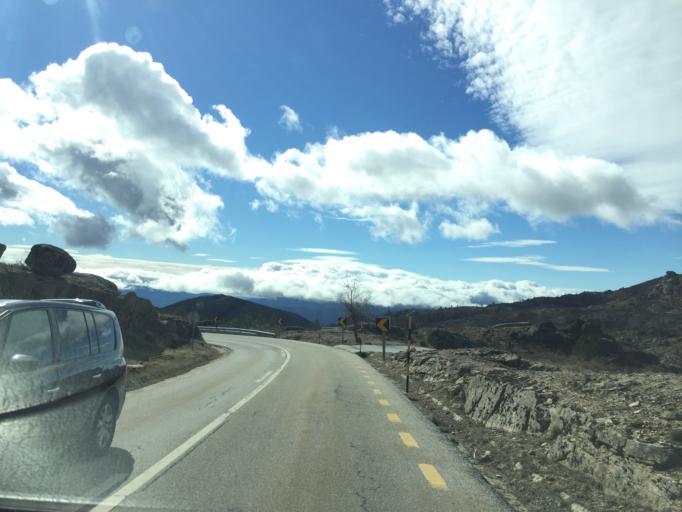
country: PT
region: Castelo Branco
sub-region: Covilha
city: Covilha
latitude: 40.3055
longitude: -7.5375
